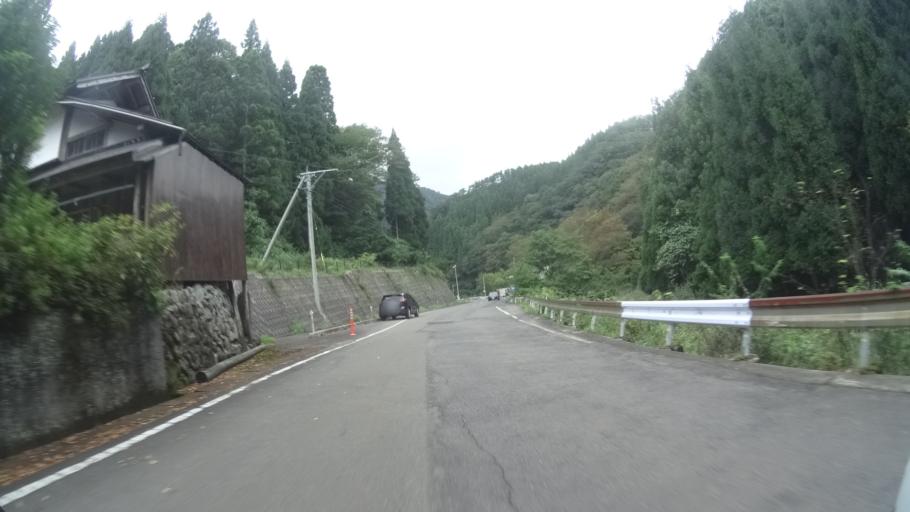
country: JP
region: Tottori
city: Kurayoshi
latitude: 35.4035
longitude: 133.9712
